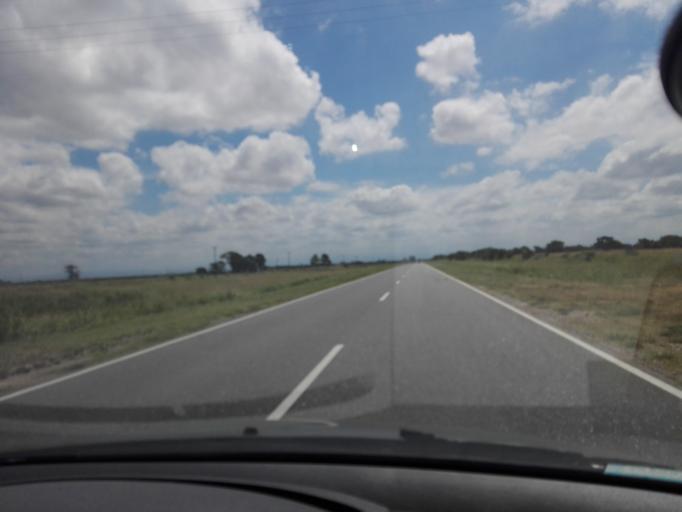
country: AR
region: Cordoba
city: Toledo
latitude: -31.6465
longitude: -64.0508
